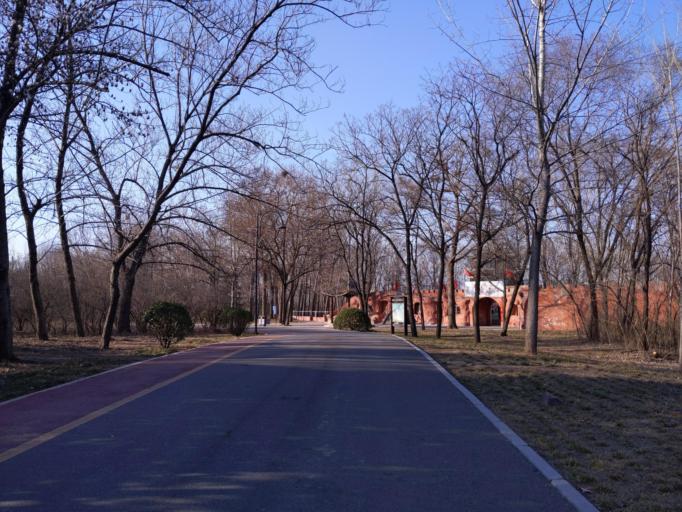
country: CN
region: Henan Sheng
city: Puyang
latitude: 35.7780
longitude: 114.9641
